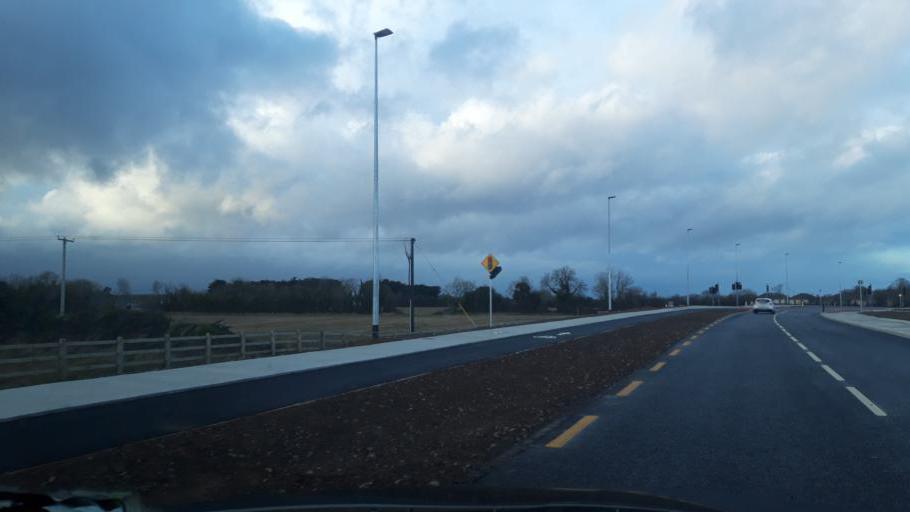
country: IE
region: Leinster
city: Donabate
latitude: 53.4866
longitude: -6.1367
